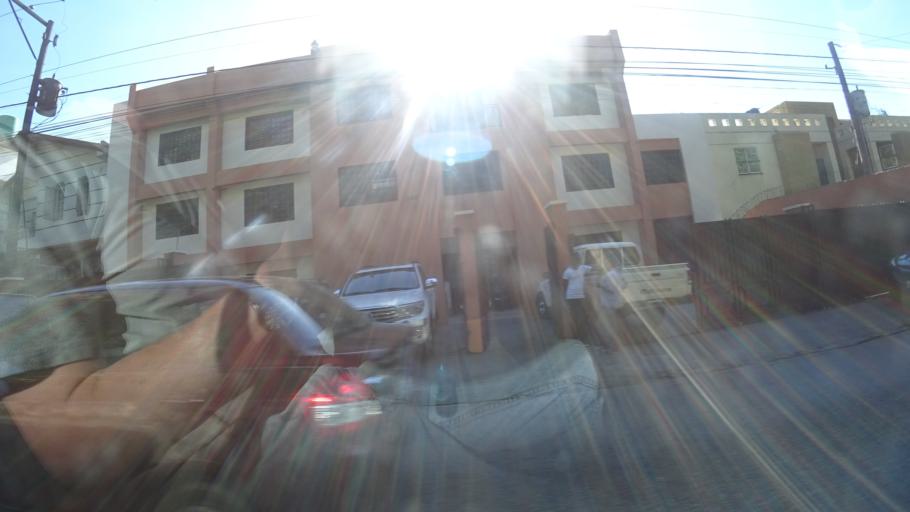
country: HT
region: Ouest
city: Delmas 73
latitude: 18.5327
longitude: -72.3037
